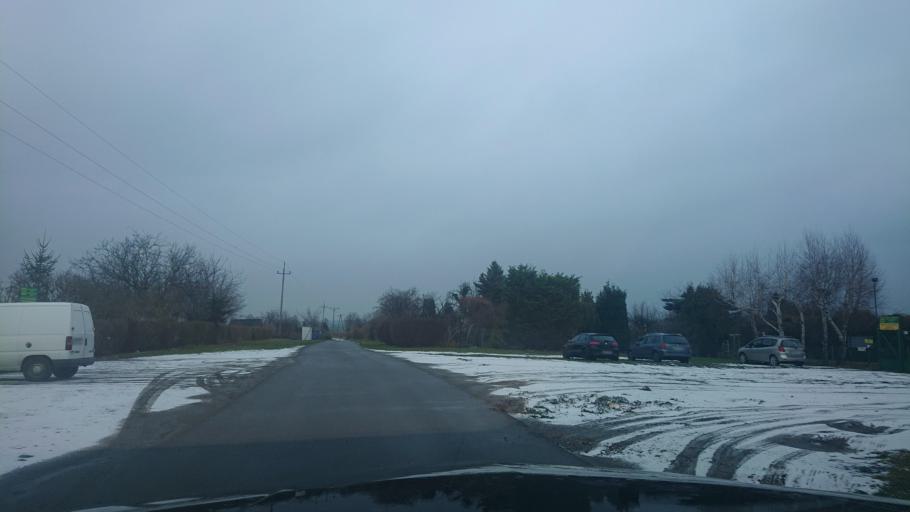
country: PL
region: Greater Poland Voivodeship
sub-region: Powiat gnieznienski
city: Gniezno
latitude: 52.5607
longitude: 17.6042
